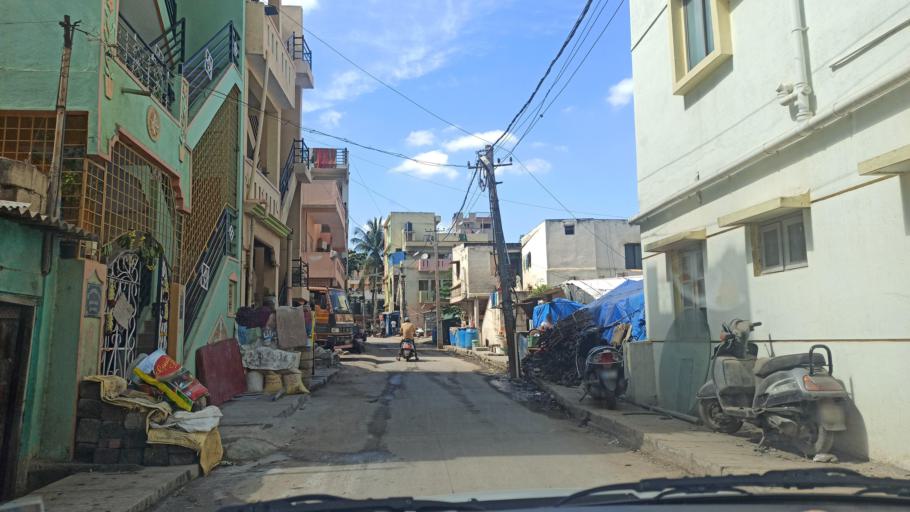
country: IN
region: Karnataka
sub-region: Bangalore Urban
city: Bangalore
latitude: 12.9231
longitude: 77.6640
